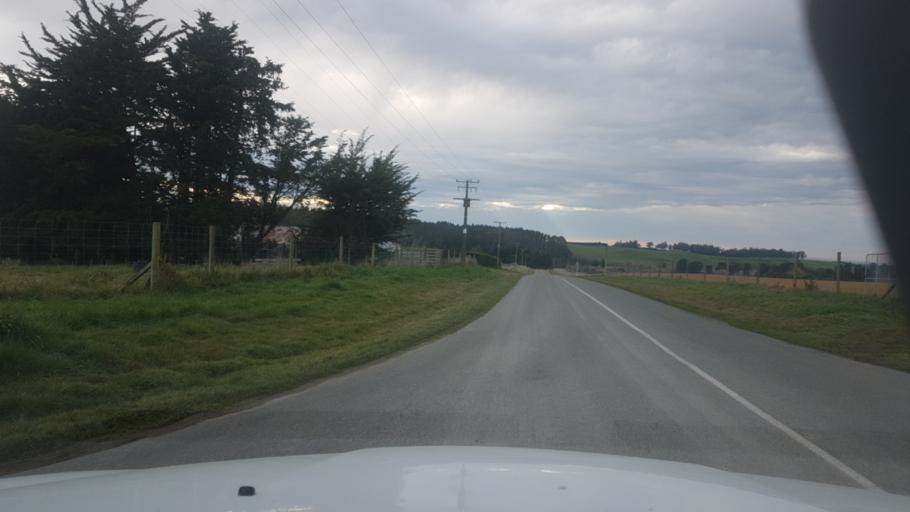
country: NZ
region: Canterbury
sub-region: Timaru District
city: Pleasant Point
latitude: -44.3320
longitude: 171.1574
